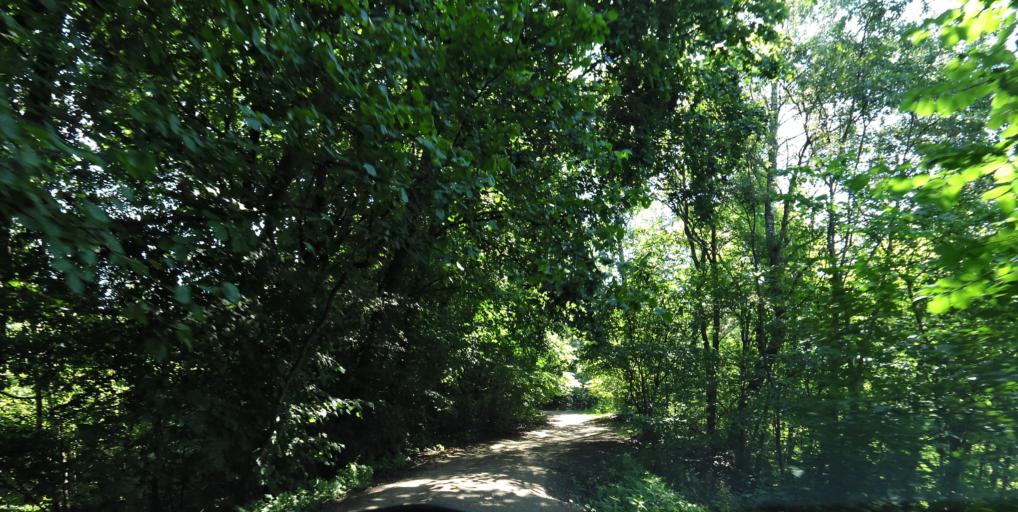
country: LT
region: Vilnius County
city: Rasos
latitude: 54.6851
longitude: 25.3597
